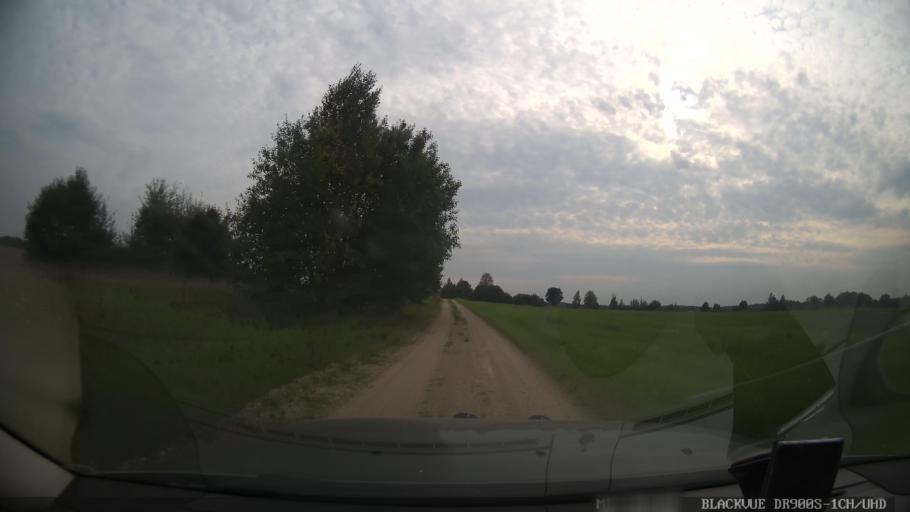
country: BY
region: Grodnenskaya
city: Ashmyany
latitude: 54.5335
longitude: 25.6714
